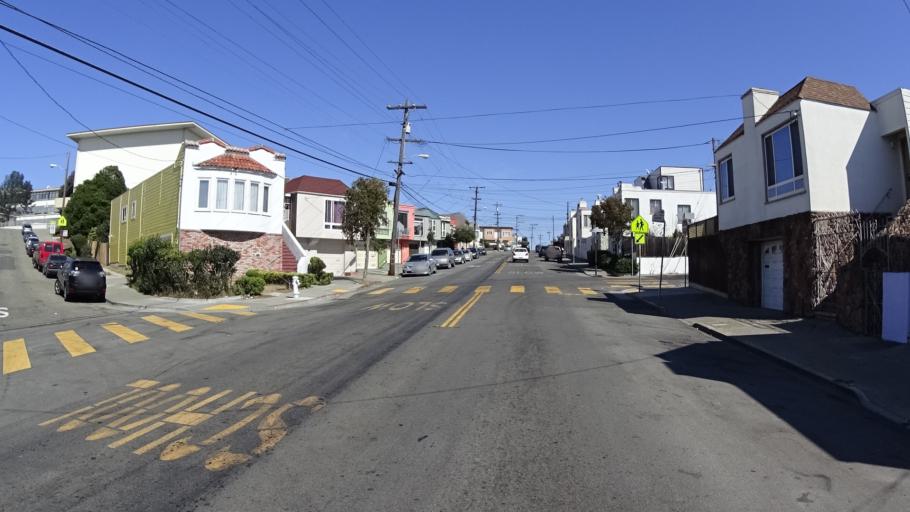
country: US
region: California
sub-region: San Francisco County
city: San Francisco
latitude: 37.7347
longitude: -122.4018
